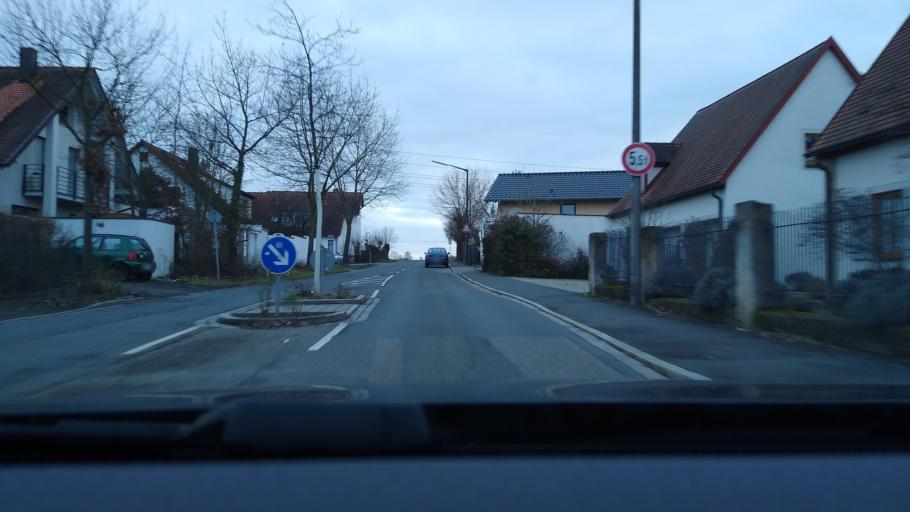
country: DE
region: Bavaria
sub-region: Regierungsbezirk Mittelfranken
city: Oberasbach
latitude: 49.4134
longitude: 10.9845
